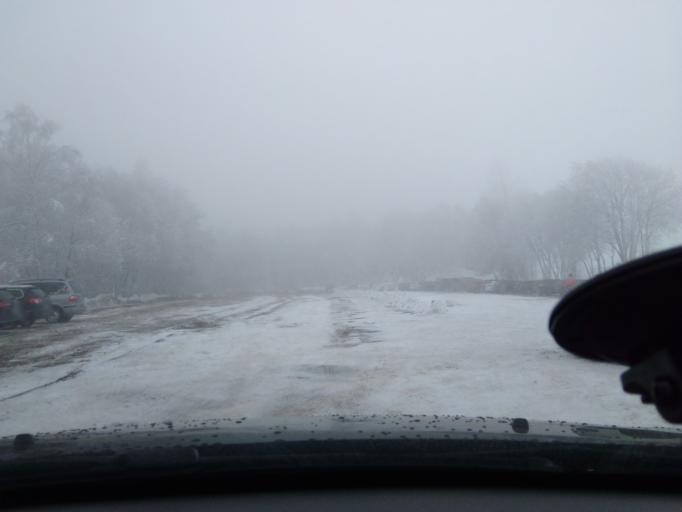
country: DE
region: Saxony
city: Markersbach
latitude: 50.5126
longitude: 12.8698
